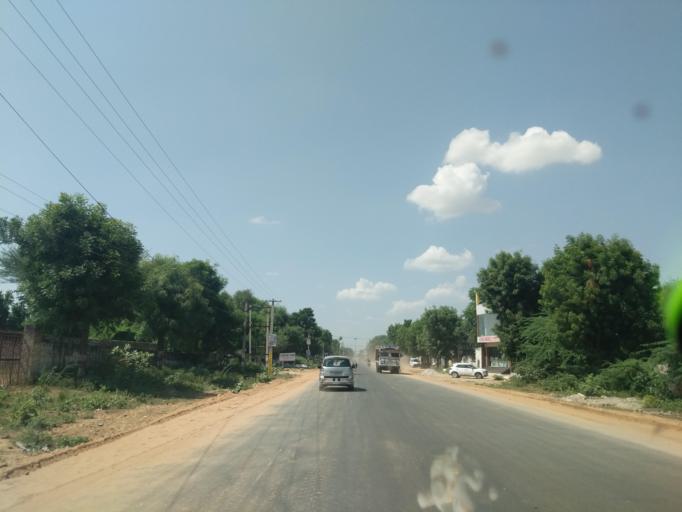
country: IN
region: Rajasthan
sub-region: Nagaur
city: Makrana
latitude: 27.0265
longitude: 74.7563
